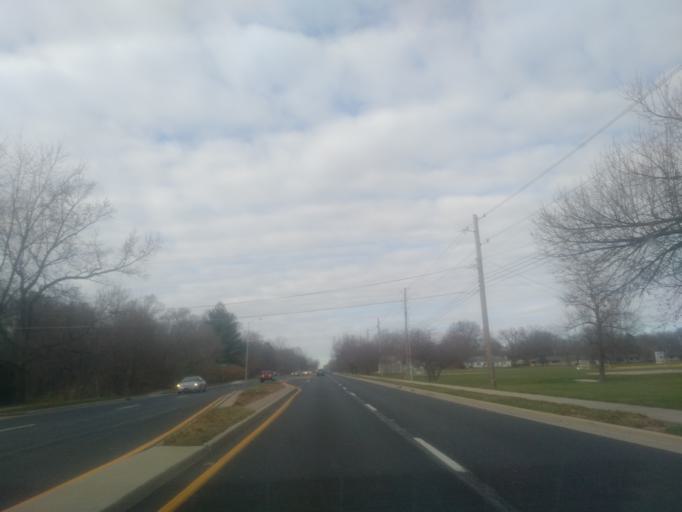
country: US
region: Indiana
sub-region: Marion County
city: Meridian Hills
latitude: 39.9125
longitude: -86.1477
